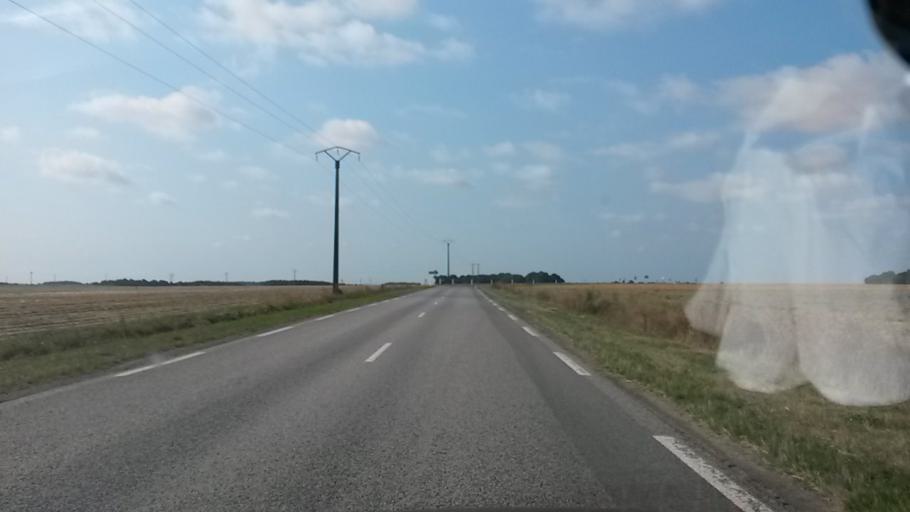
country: FR
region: Haute-Normandie
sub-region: Departement de l'Eure
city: Tillieres-sur-Avre
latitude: 48.8041
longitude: 0.9987
